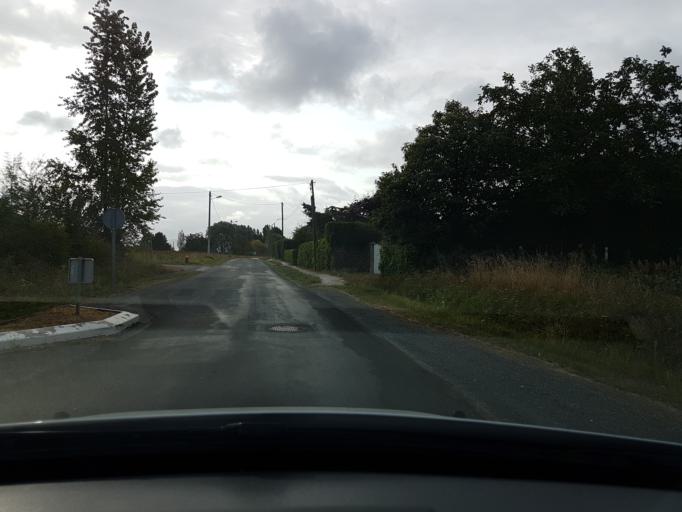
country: FR
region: Centre
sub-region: Departement d'Indre-et-Loire
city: Larcay
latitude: 47.3483
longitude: 0.7742
